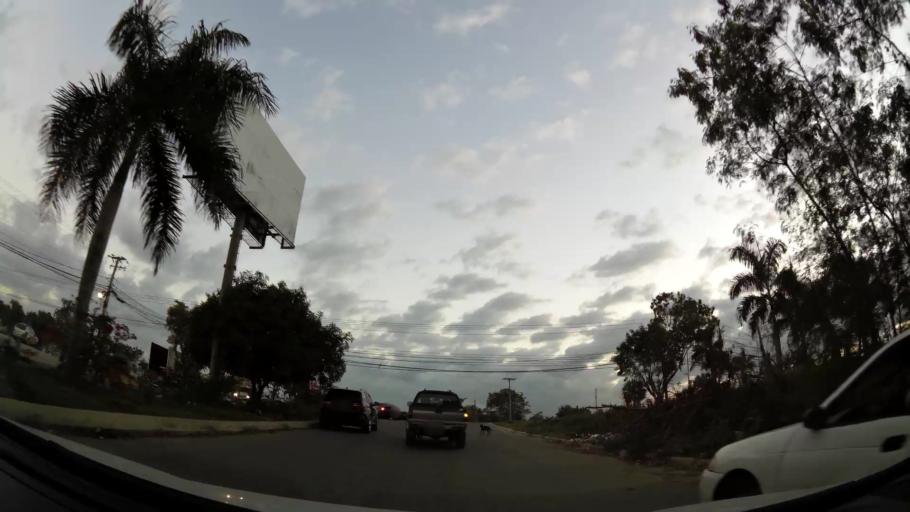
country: DO
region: Nacional
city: La Agustina
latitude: 18.5566
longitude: -69.9391
